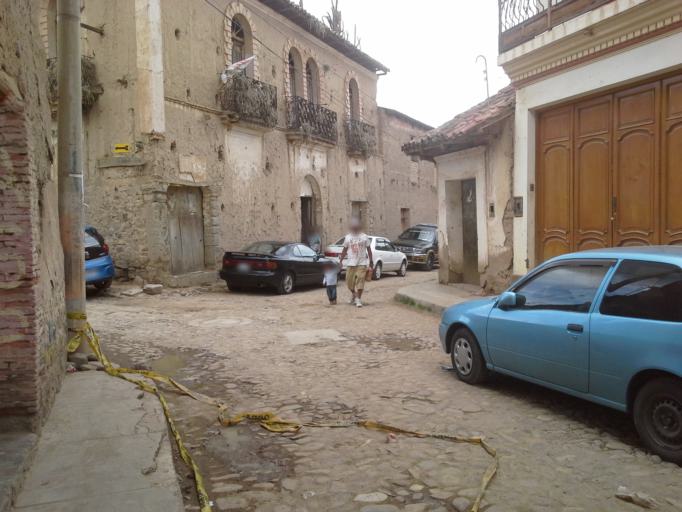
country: BO
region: Cochabamba
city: Tarata
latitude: -17.6111
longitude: -66.0229
